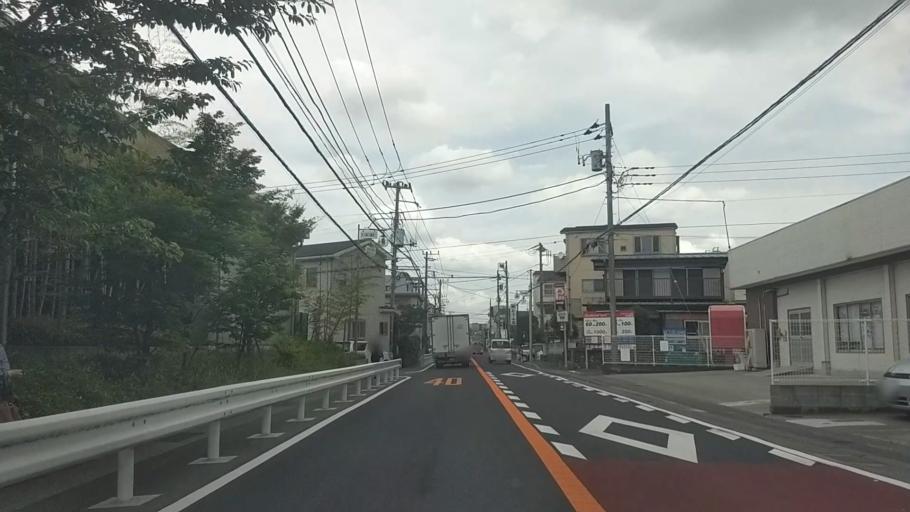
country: JP
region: Kanagawa
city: Fujisawa
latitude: 35.3286
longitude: 139.5094
